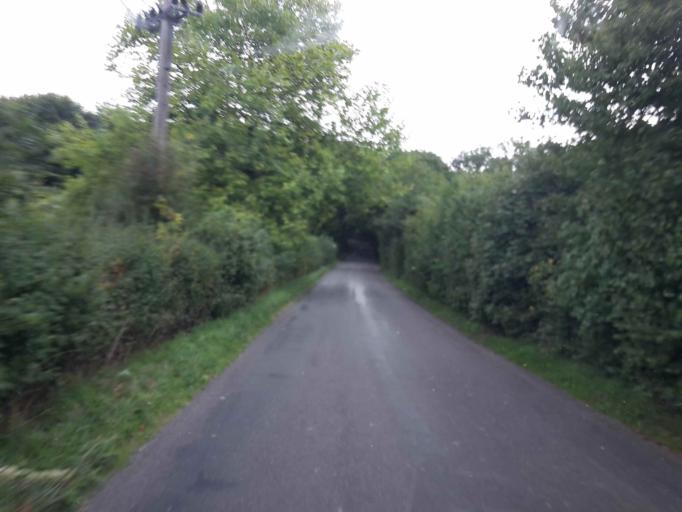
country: GB
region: England
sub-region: West Sussex
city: Billingshurst
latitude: 51.0305
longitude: -0.4367
